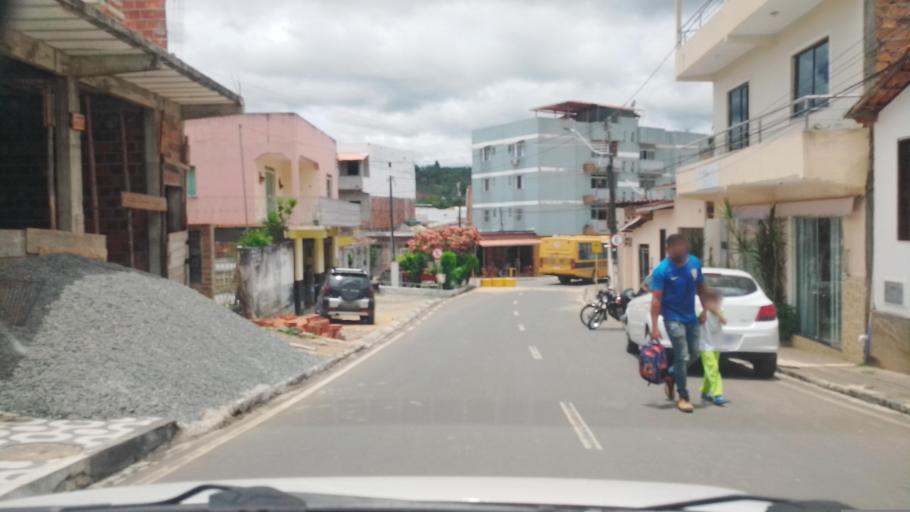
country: BR
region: Bahia
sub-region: Mutuipe
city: Mutuipe
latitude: -13.2586
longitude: -39.5691
